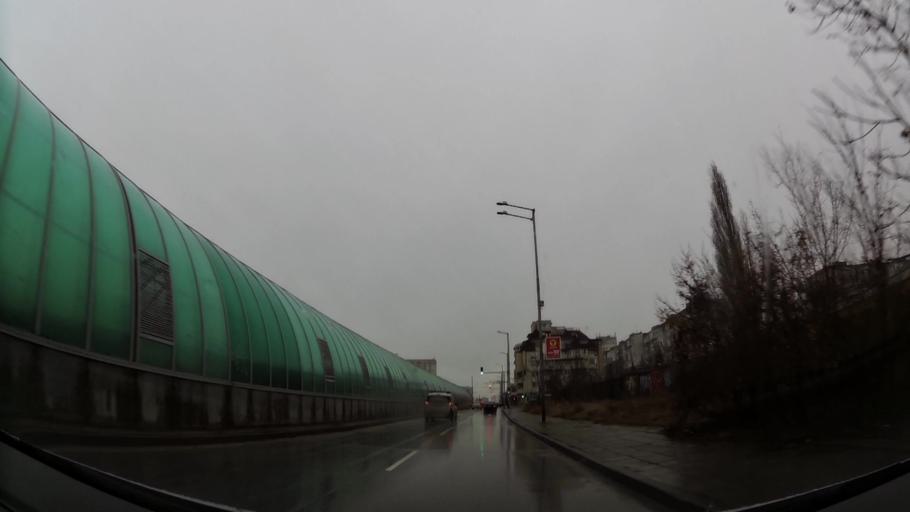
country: BG
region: Sofia-Capital
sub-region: Stolichna Obshtina
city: Sofia
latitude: 42.6555
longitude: 23.3696
